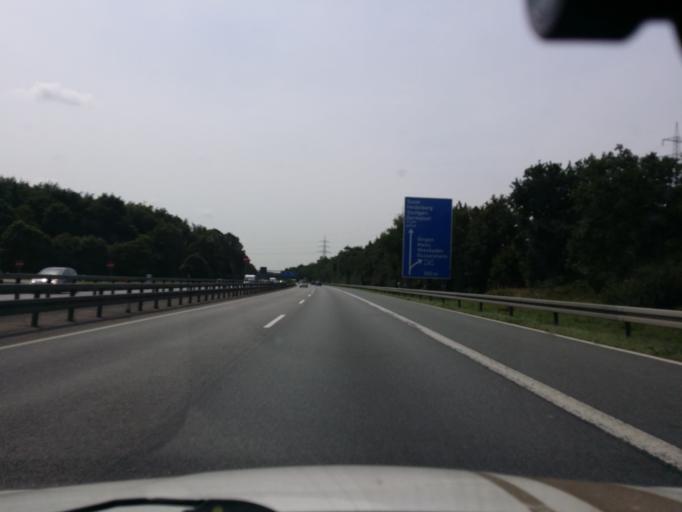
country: DE
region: Hesse
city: Raunheim
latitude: 49.9893
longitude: 8.4676
